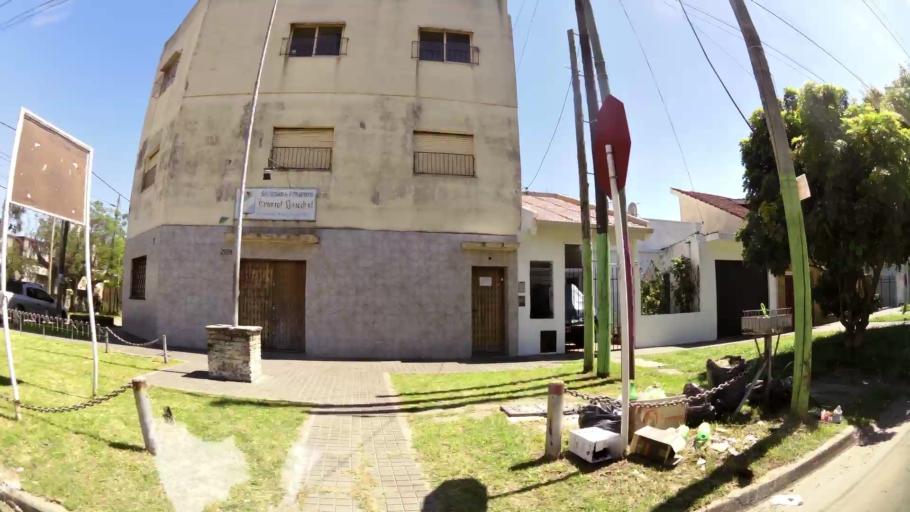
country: AR
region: Buenos Aires
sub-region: Partido de Quilmes
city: Quilmes
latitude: -34.7272
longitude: -58.2870
